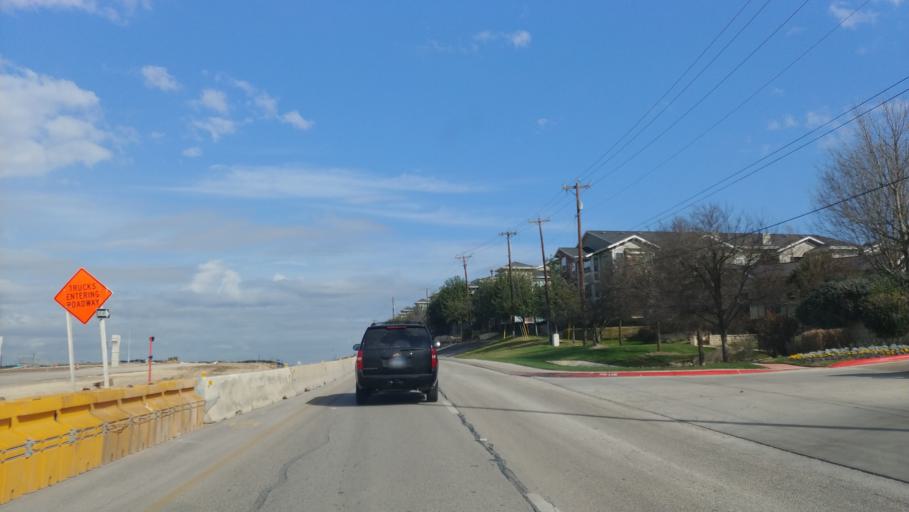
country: US
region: Texas
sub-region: Bexar County
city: Leon Valley
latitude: 29.4613
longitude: -98.7110
